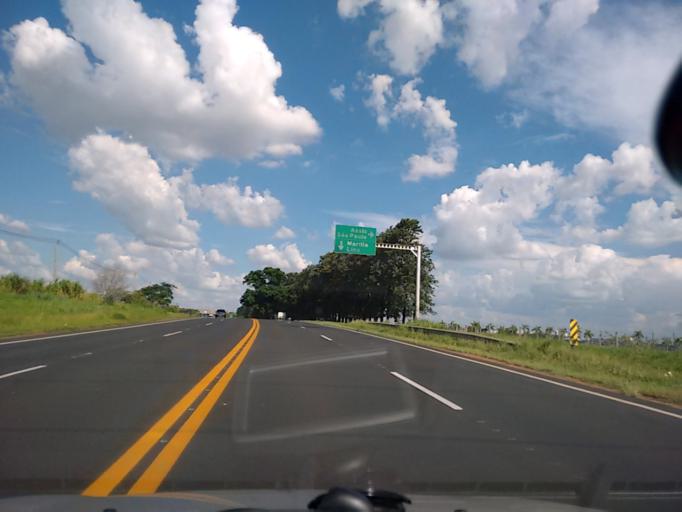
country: BR
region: Sao Paulo
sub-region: Marilia
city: Marilia
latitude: -22.1754
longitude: -49.9787
